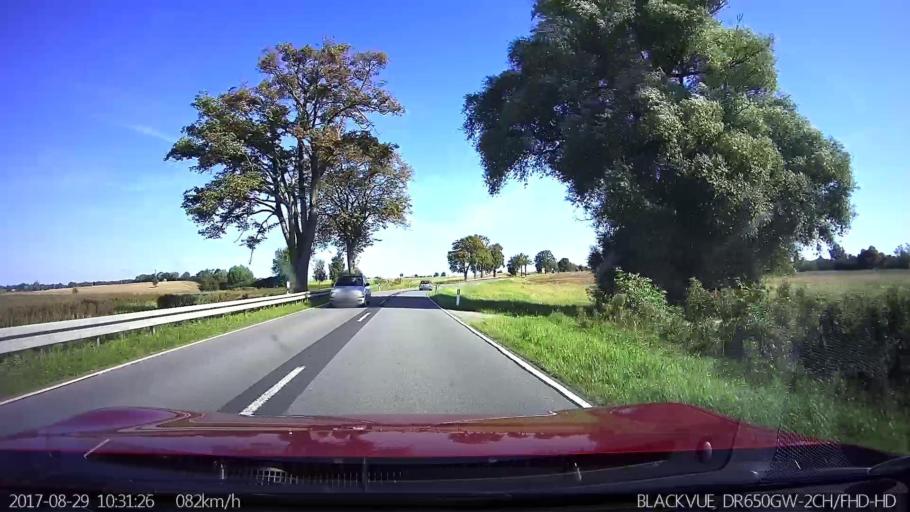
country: DE
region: Mecklenburg-Vorpommern
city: Tribsees
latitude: 54.0986
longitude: 12.7521
